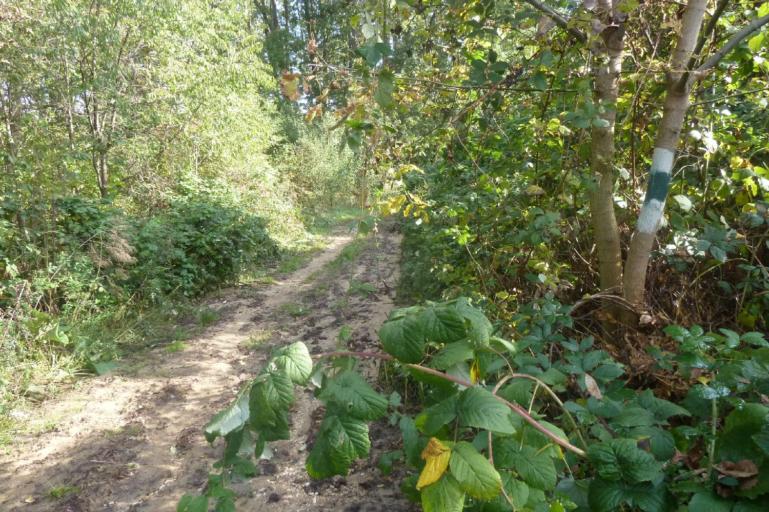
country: HU
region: Pest
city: Solymar
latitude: 47.5890
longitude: 18.9153
